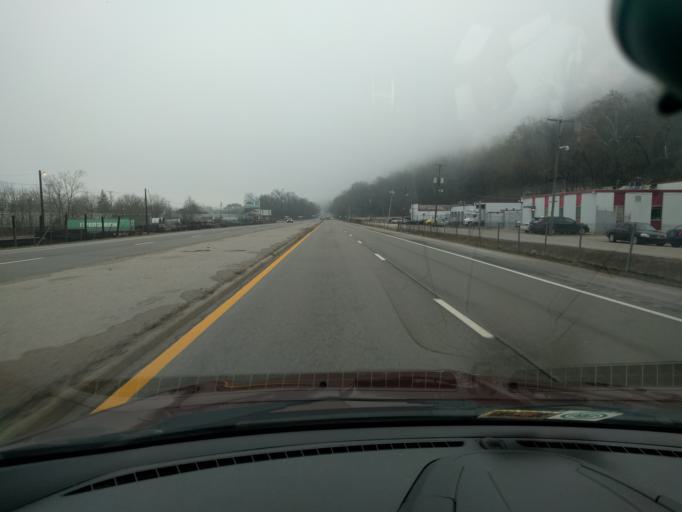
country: US
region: West Virginia
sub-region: Kanawha County
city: Rand
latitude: 38.2868
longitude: -81.5611
